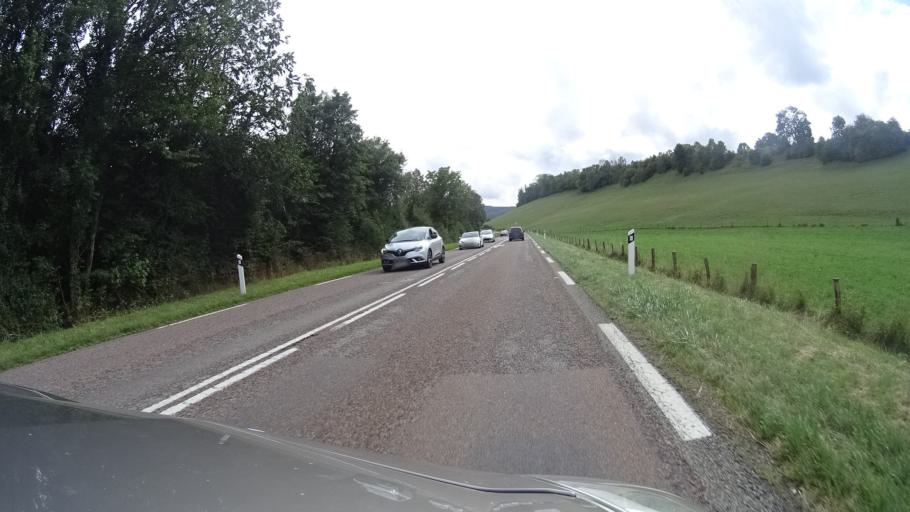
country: FR
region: Franche-Comte
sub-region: Departement du Jura
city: Champagnole
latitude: 46.7000
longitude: 5.9312
